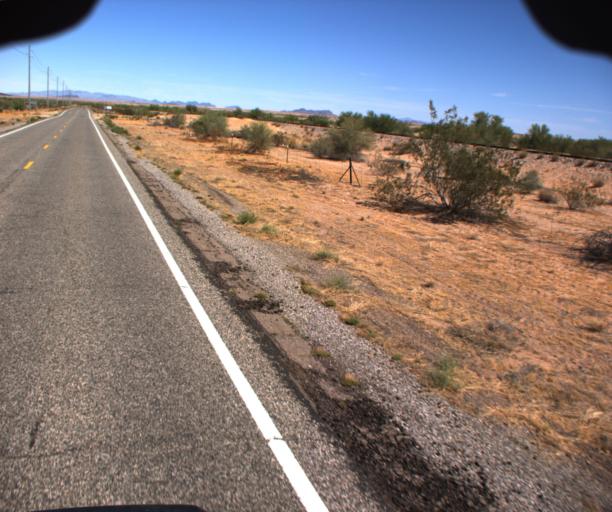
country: US
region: Arizona
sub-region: La Paz County
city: Cienega Springs
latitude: 33.9660
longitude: -114.0372
